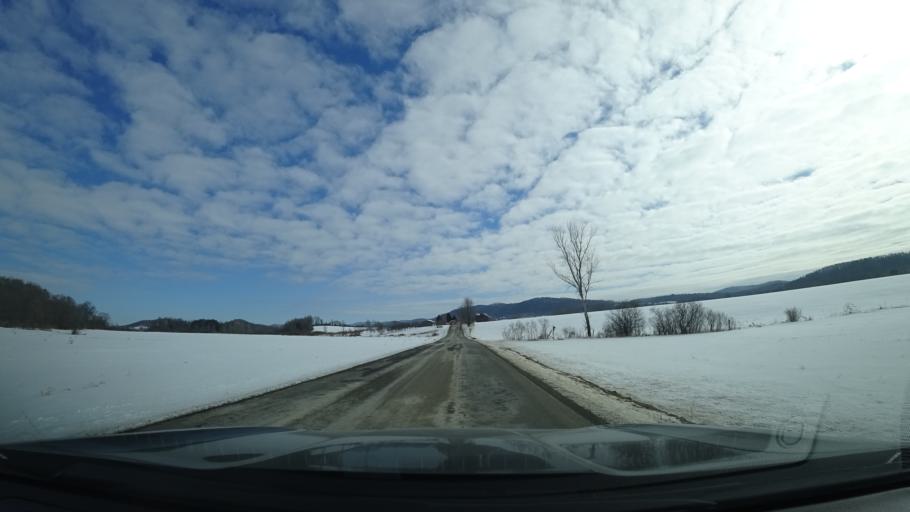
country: US
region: New York
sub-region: Washington County
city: Fort Edward
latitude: 43.2522
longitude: -73.4840
